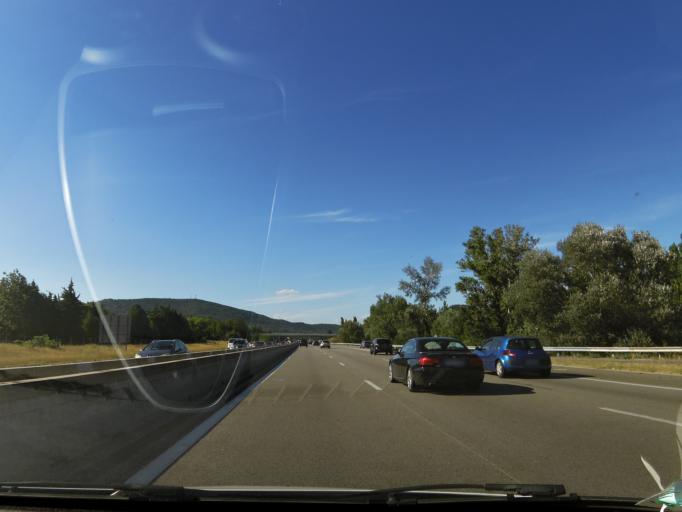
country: FR
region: Rhone-Alpes
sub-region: Departement de la Drome
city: Saint-Marcel-les-Sauzet
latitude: 44.5914
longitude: 4.8000
